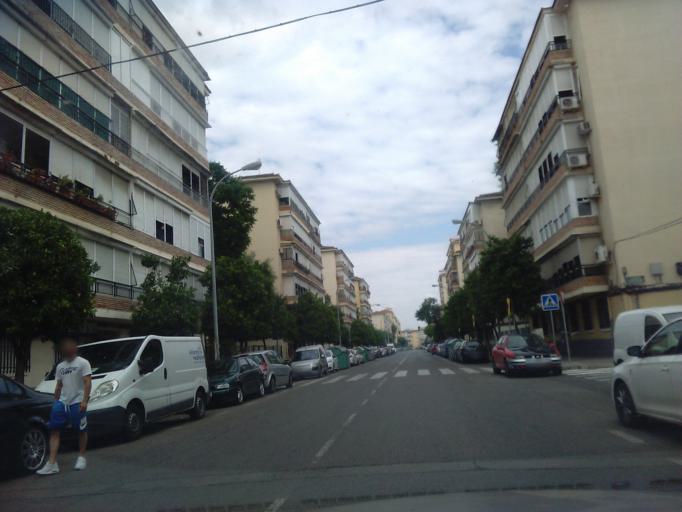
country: ES
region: Andalusia
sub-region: Provincia de Sevilla
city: Sevilla
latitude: 37.4109
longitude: -5.9282
